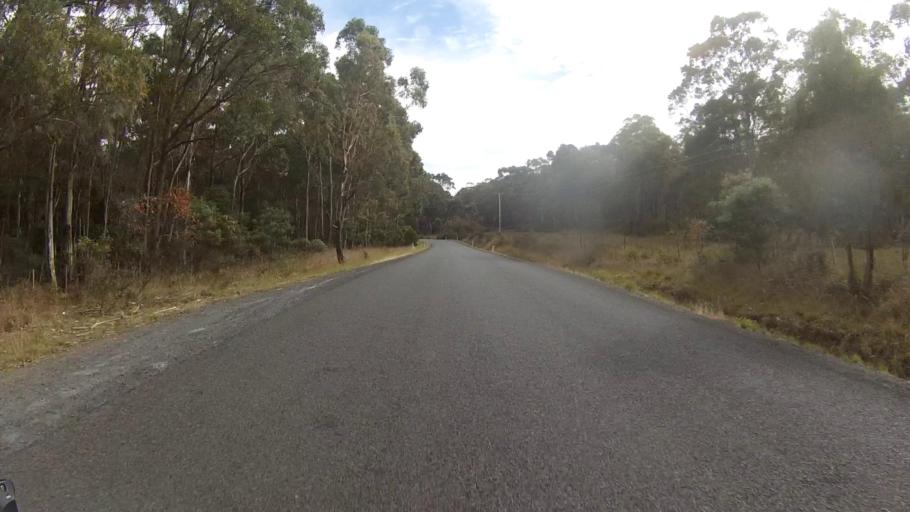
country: AU
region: Tasmania
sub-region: Sorell
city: Sorell
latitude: -42.8156
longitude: 147.7916
